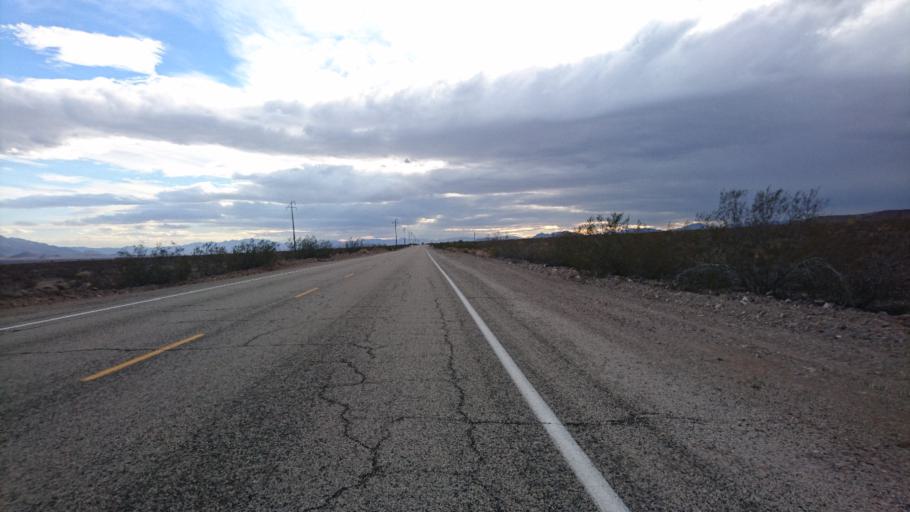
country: US
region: California
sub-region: San Bernardino County
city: Needles
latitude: 34.6619
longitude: -115.3523
